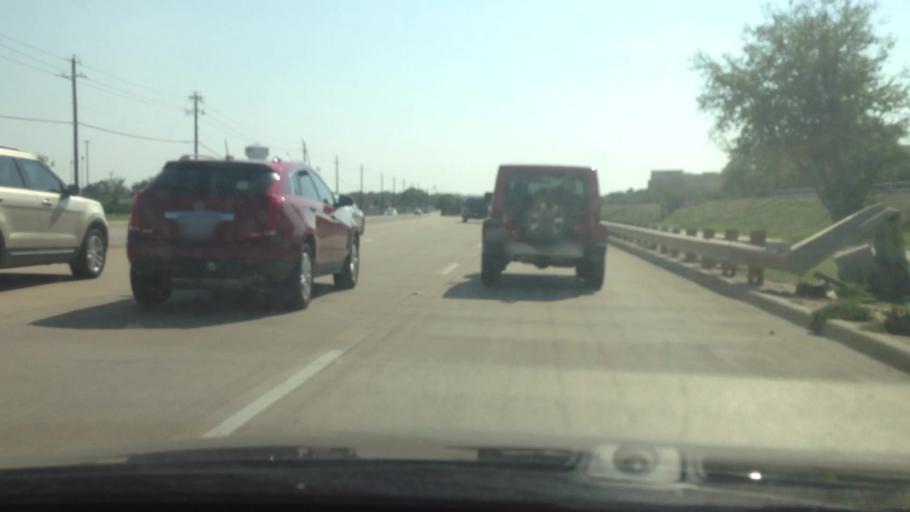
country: US
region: Texas
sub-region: Tarrant County
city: Southlake
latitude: 32.9263
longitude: -97.1089
